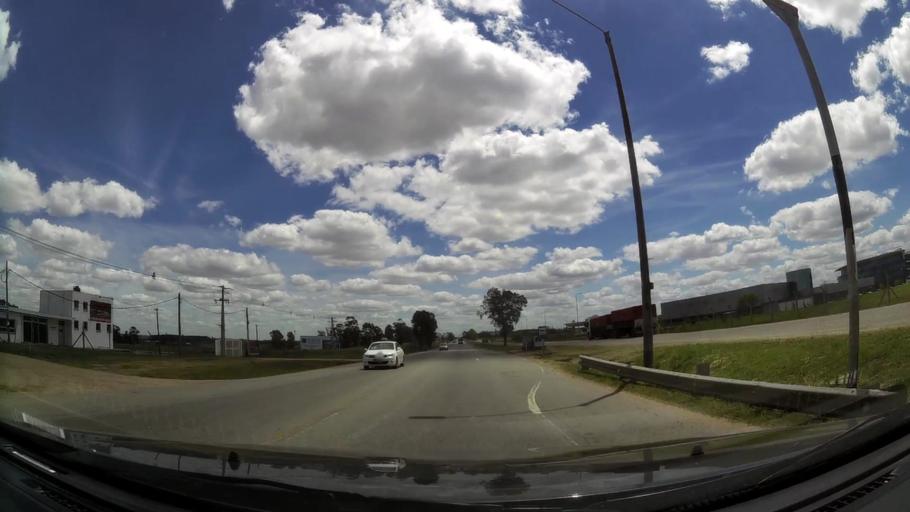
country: UY
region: Canelones
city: Colonia Nicolich
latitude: -34.8156
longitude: -56.0075
